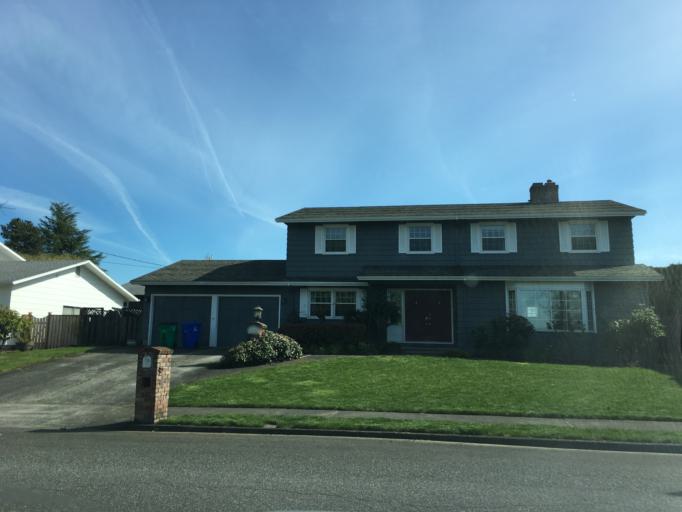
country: US
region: Oregon
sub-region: Multnomah County
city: Lents
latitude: 45.5440
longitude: -122.5294
